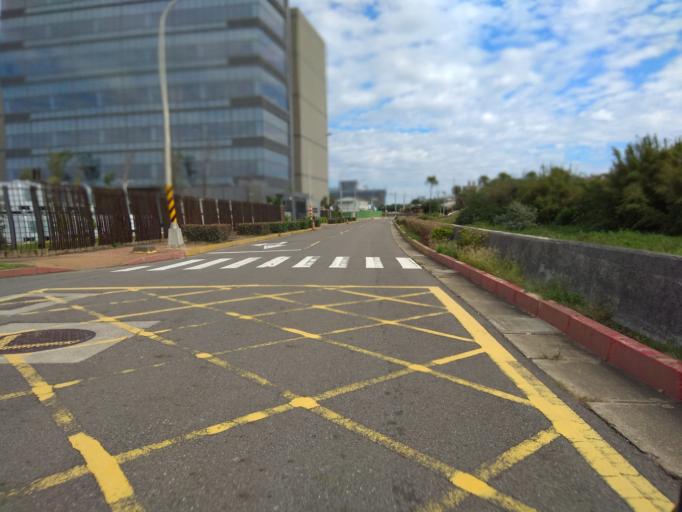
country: TW
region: Taiwan
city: Taoyuan City
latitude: 25.0476
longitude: 121.0884
